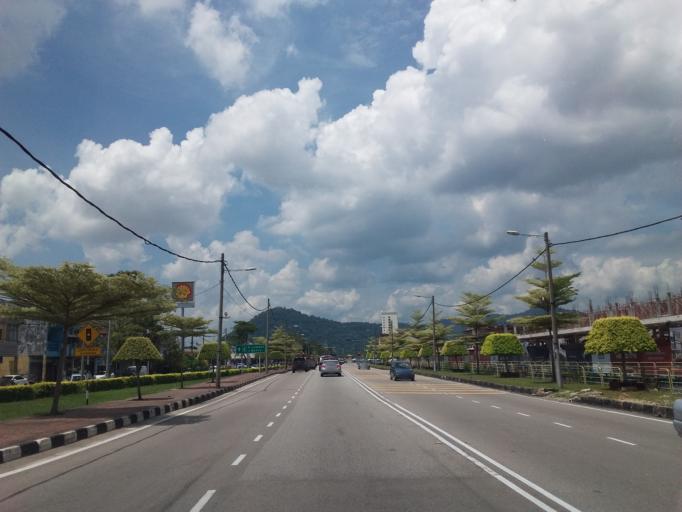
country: MY
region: Johor
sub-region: Daerah Batu Pahat
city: Batu Pahat
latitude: 1.8595
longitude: 102.9288
